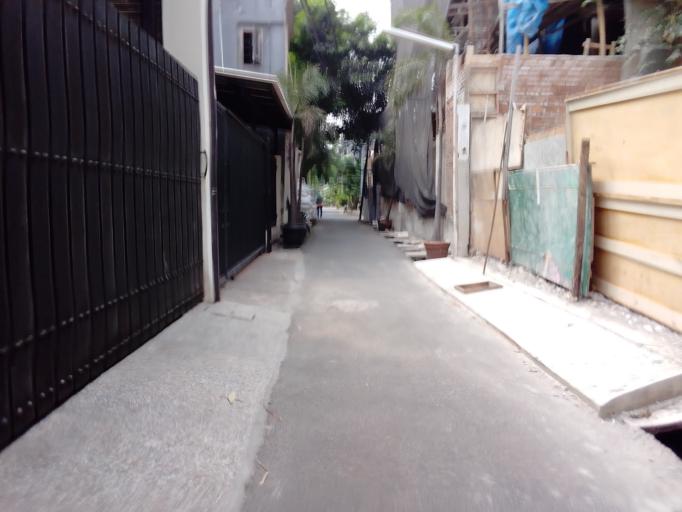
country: ID
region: Jakarta Raya
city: Jakarta
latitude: -6.1634
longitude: 106.8099
